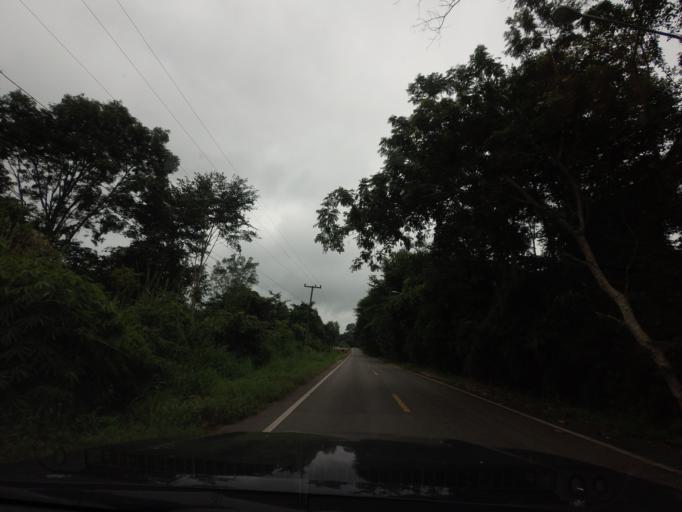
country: TH
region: Nong Khai
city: Sangkhom
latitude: 18.0265
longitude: 102.3593
